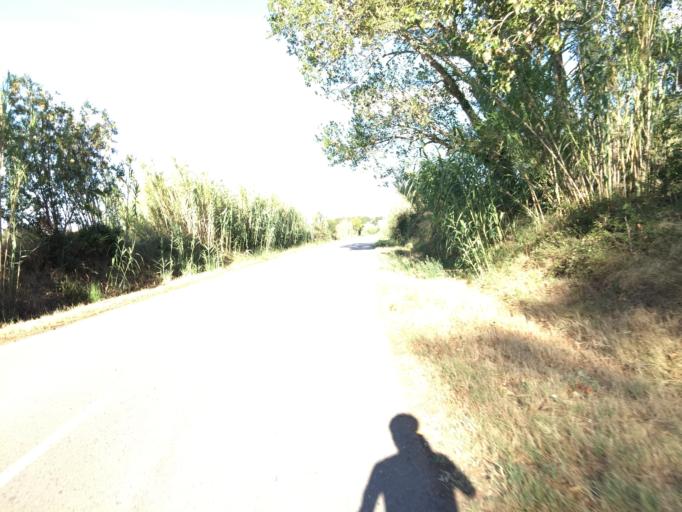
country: ES
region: Catalonia
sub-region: Provincia de Girona
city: Vilajuiga
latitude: 42.3127
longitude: 3.0752
